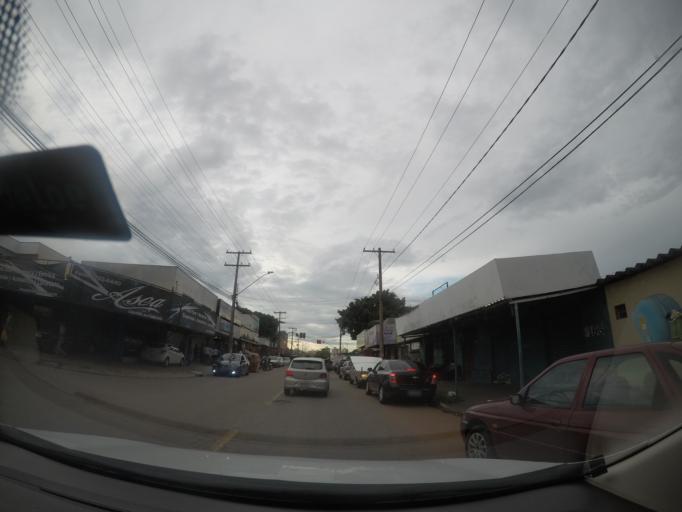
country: BR
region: Goias
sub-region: Goiania
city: Goiania
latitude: -16.6571
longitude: -49.2534
